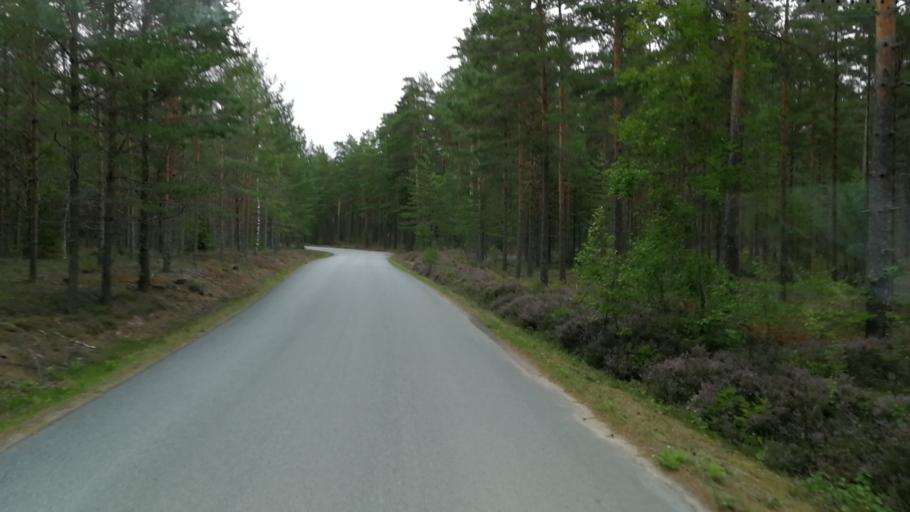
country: SE
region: Vaermland
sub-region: Hammaro Kommun
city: Skoghall
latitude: 59.3628
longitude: 13.3633
